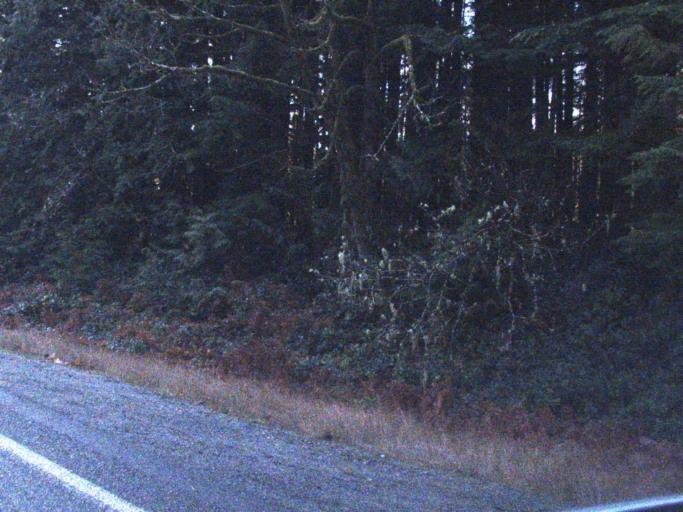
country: US
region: Washington
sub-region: Snohomish County
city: Darrington
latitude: 48.4044
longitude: -121.5556
